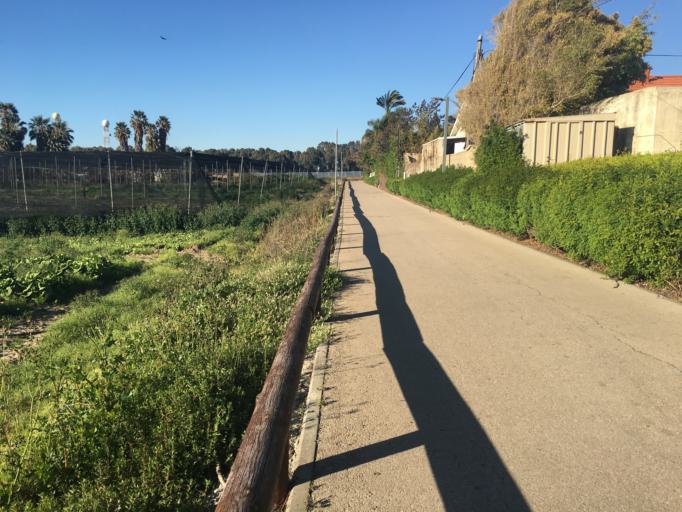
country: IL
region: Tel Aviv
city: Ramat HaSharon
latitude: 32.1409
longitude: 34.8234
